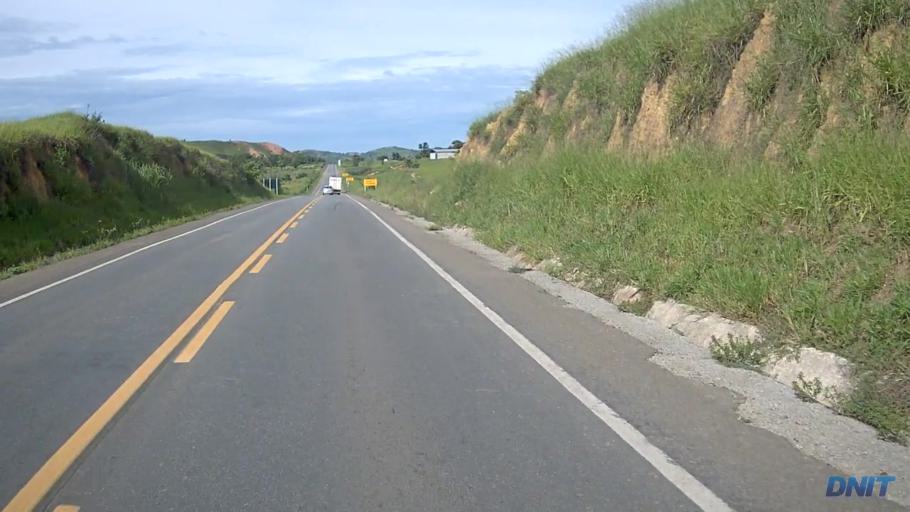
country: BR
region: Minas Gerais
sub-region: Belo Oriente
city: Belo Oriente
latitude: -19.1936
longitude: -42.2778
